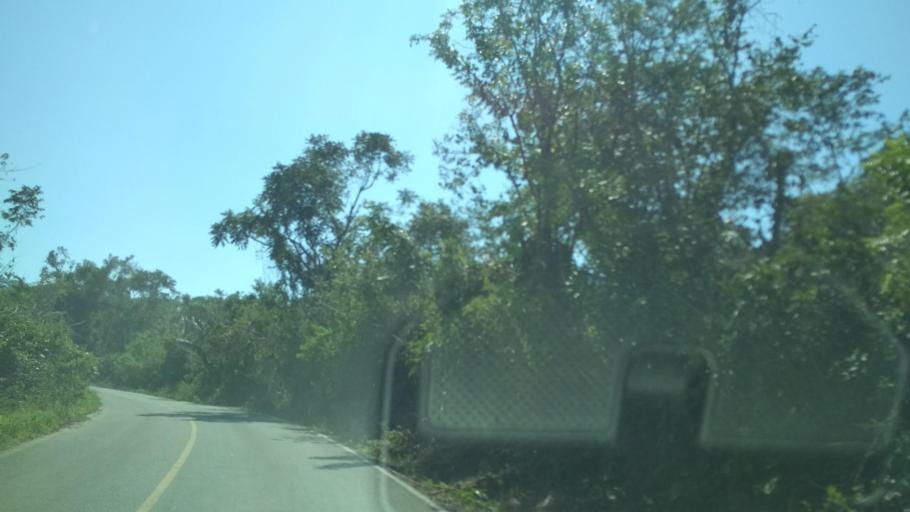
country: MX
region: Veracruz
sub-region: Papantla
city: Polutla
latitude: 20.4699
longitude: -97.2256
